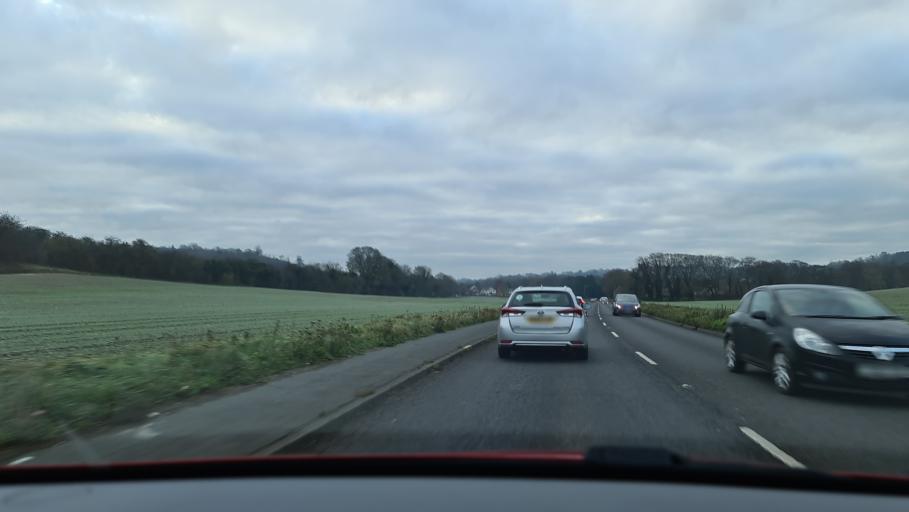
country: GB
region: England
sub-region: Buckinghamshire
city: High Wycombe
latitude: 51.6504
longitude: -0.7981
